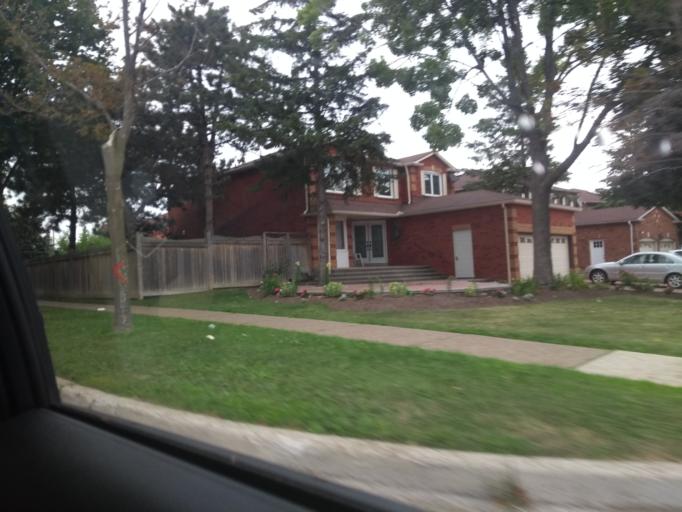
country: CA
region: Ontario
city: Mississauga
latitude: 43.6136
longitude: -79.6594
